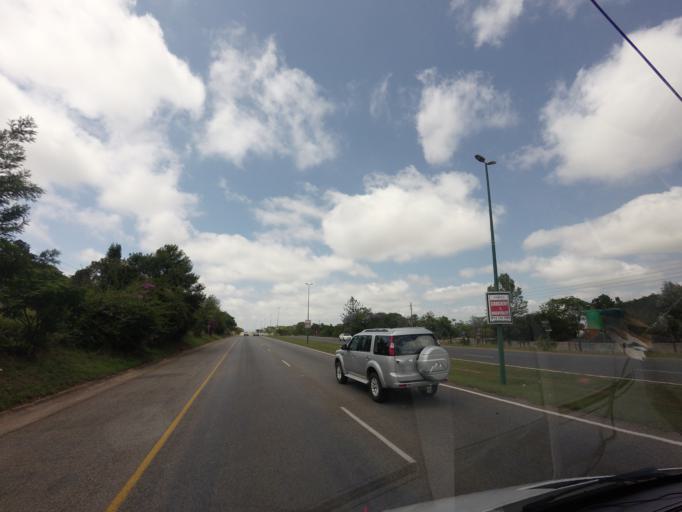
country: ZA
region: Mpumalanga
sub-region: Ehlanzeni District
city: White River
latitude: -25.3477
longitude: 30.9992
